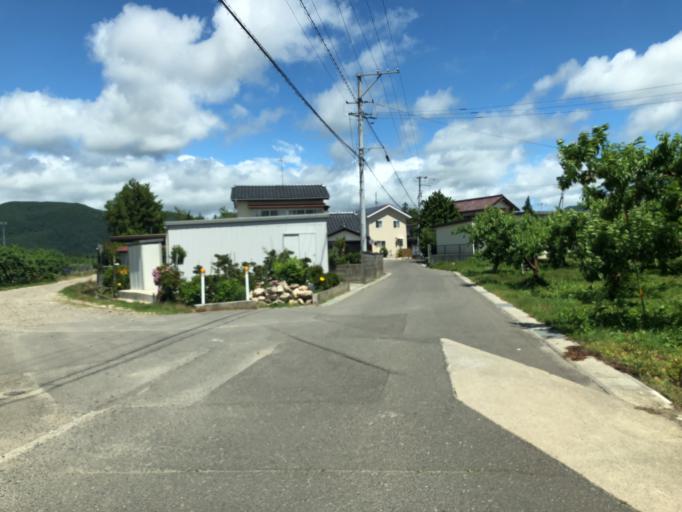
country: JP
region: Fukushima
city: Fukushima-shi
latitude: 37.8023
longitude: 140.4362
